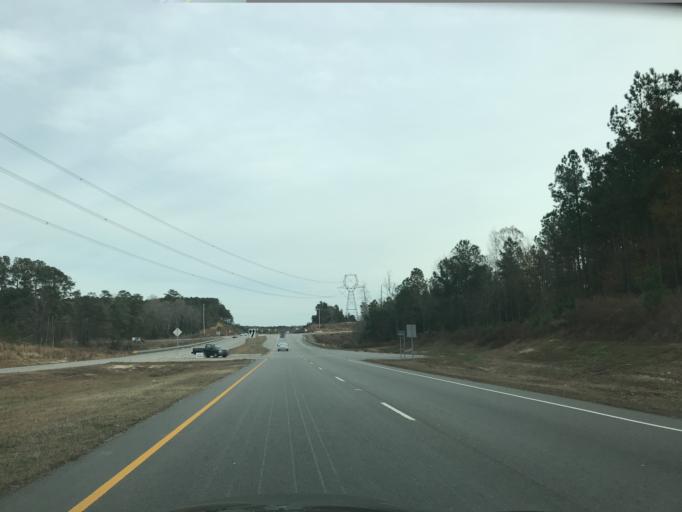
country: US
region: North Carolina
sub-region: Wake County
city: Rolesville
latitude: 35.9009
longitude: -78.4821
